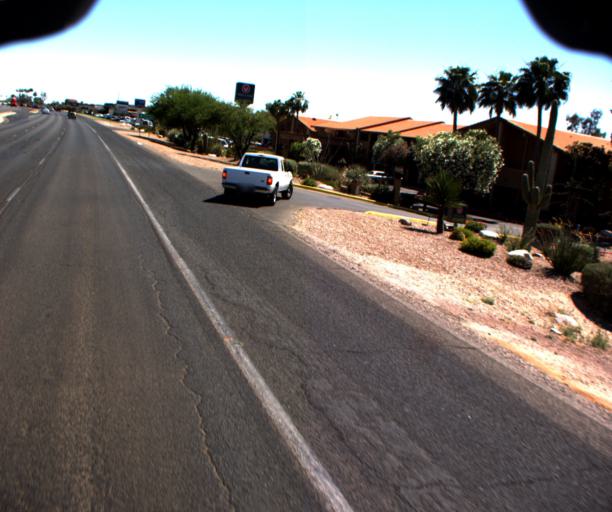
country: US
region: Arizona
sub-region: Pima County
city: Casas Adobes
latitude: 32.3421
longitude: -110.9771
